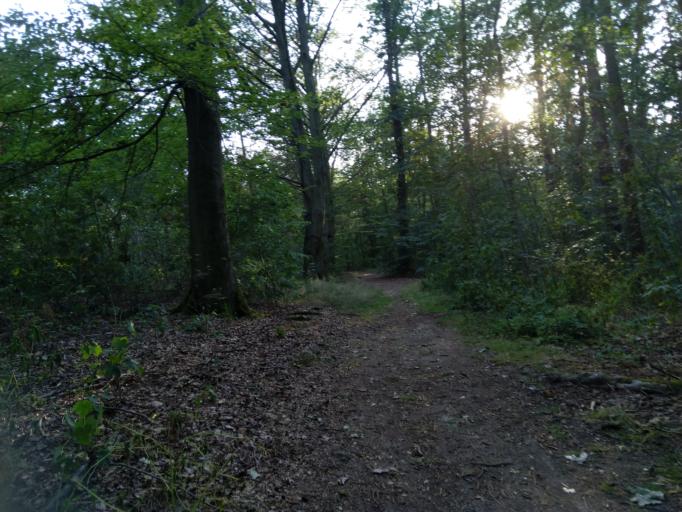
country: DE
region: Saxony
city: Brandis
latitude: 51.3173
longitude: 12.6095
